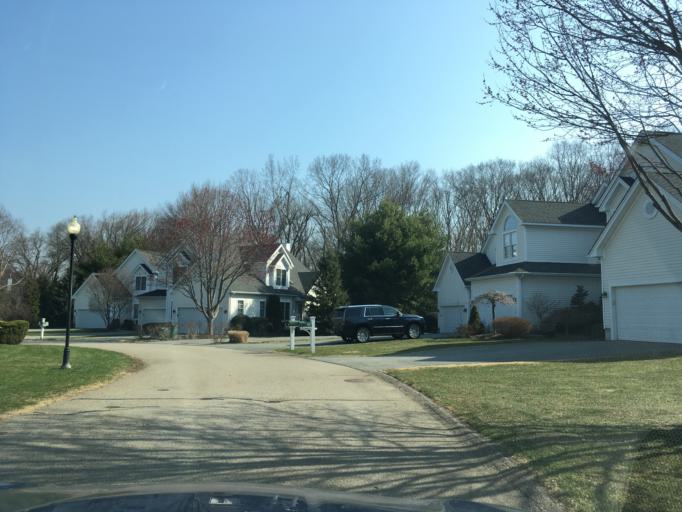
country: US
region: Rhode Island
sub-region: Kent County
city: East Greenwich
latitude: 41.6575
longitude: -71.4815
